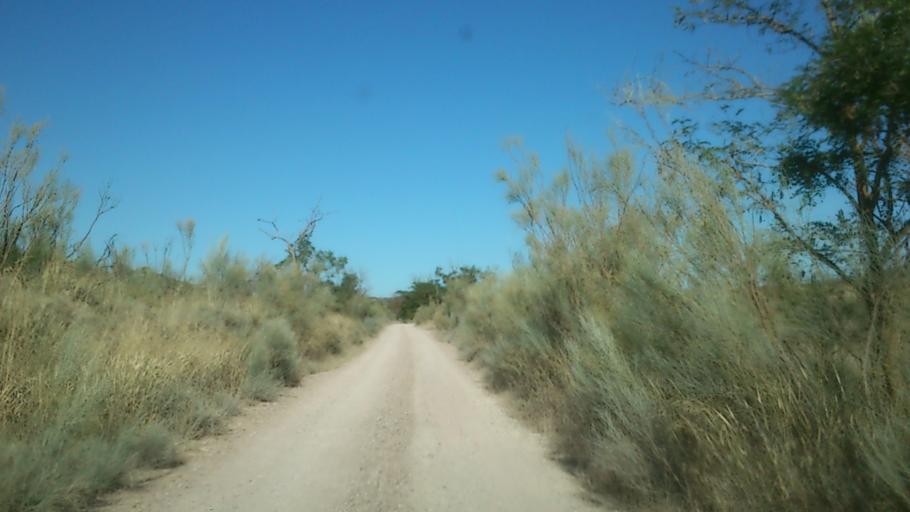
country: ES
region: Aragon
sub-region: Provincia de Zaragoza
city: San Mateo de Gallego
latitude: 41.7680
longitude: -0.7538
